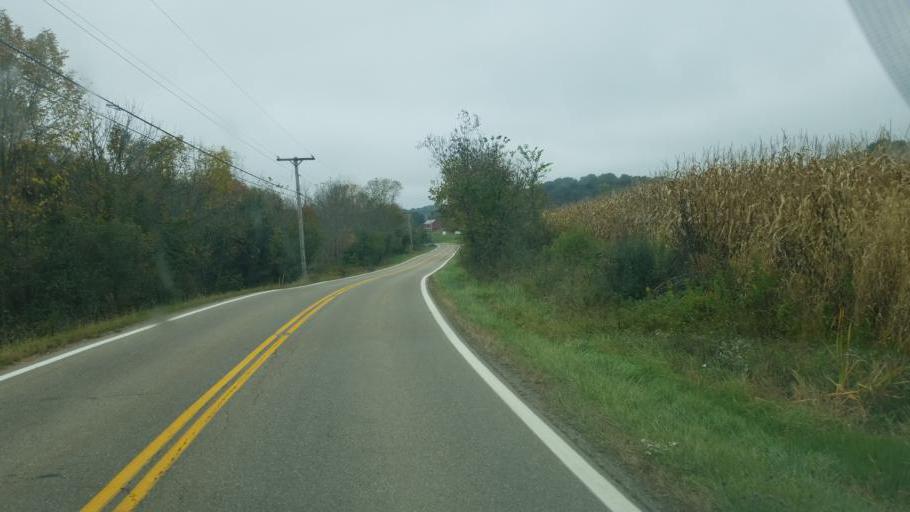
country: US
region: Ohio
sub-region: Tuscarawas County
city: Strasburg
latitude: 40.6544
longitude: -81.5176
